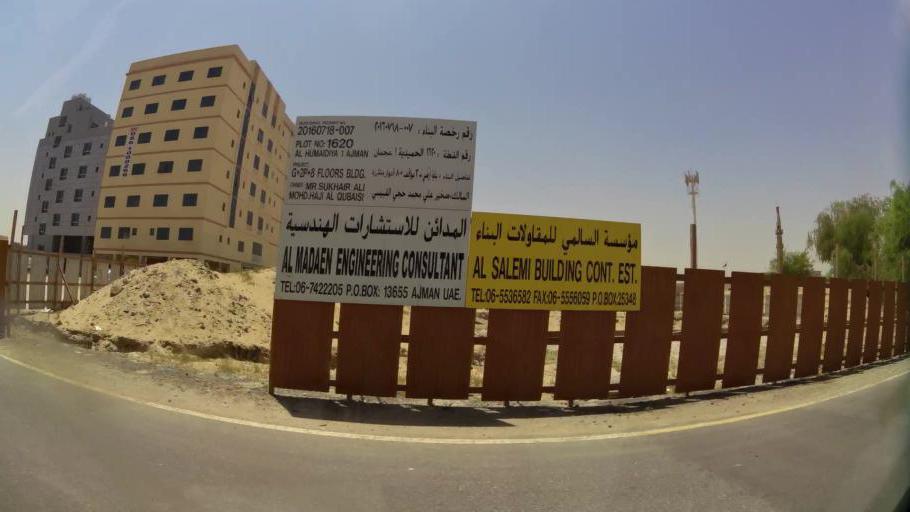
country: AE
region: Ajman
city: Ajman
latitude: 25.4059
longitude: 55.5143
